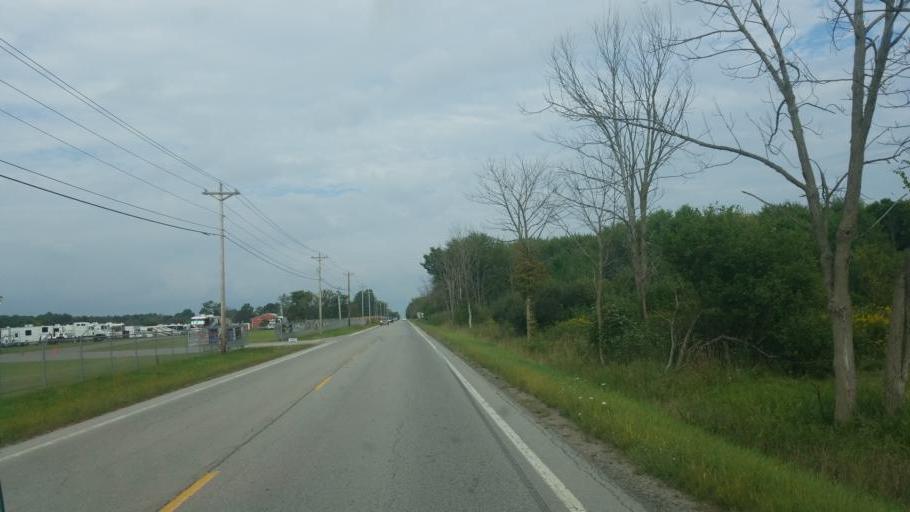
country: US
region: Ohio
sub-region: Wayne County
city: West Salem
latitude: 40.9824
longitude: -82.0951
